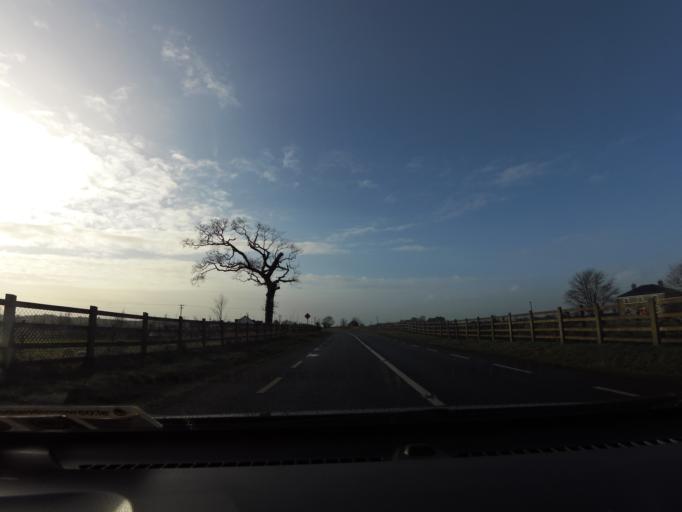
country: IE
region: Connaught
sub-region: County Galway
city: Tuam
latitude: 53.4917
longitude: -8.9726
